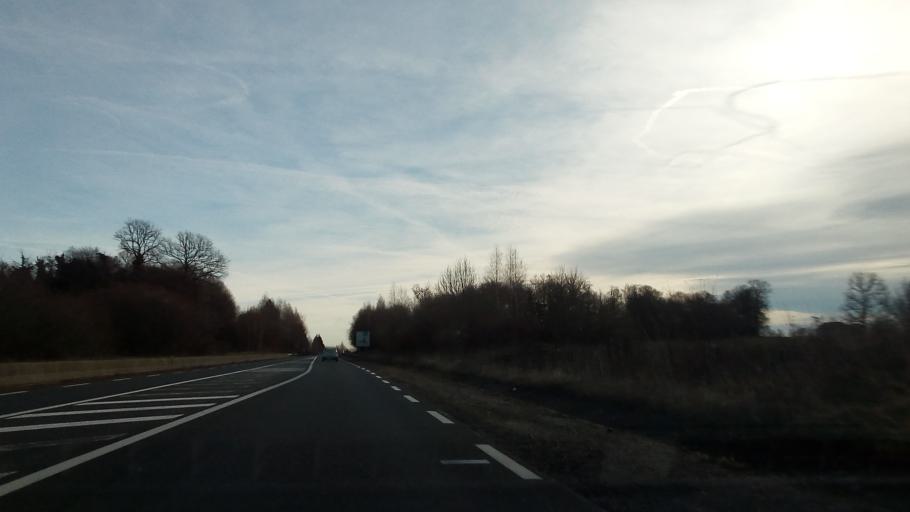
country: FR
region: Limousin
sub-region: Departement de la Correze
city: Seilhac
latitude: 45.3563
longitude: 1.7252
